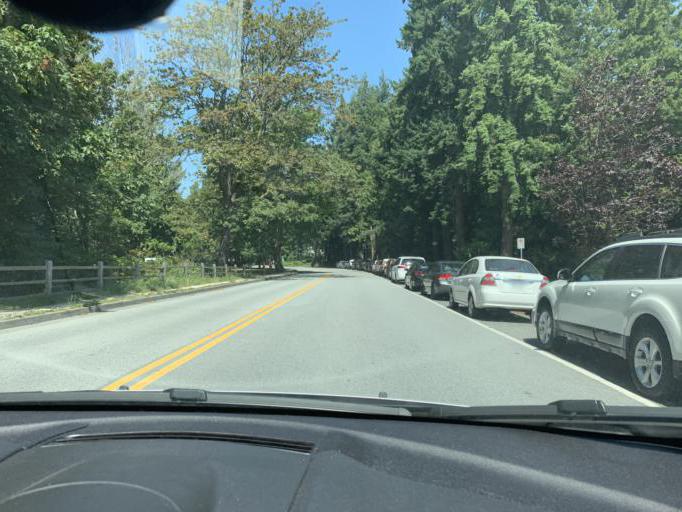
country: CA
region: British Columbia
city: West End
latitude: 49.2585
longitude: -123.2545
